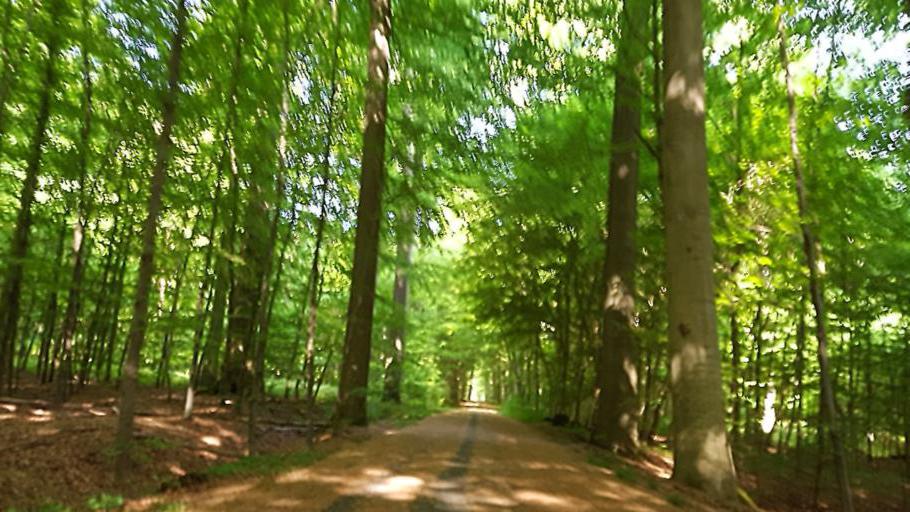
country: BE
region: Flanders
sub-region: Provincie Vlaams-Brabant
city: Tervuren
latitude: 50.8106
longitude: 4.5272
